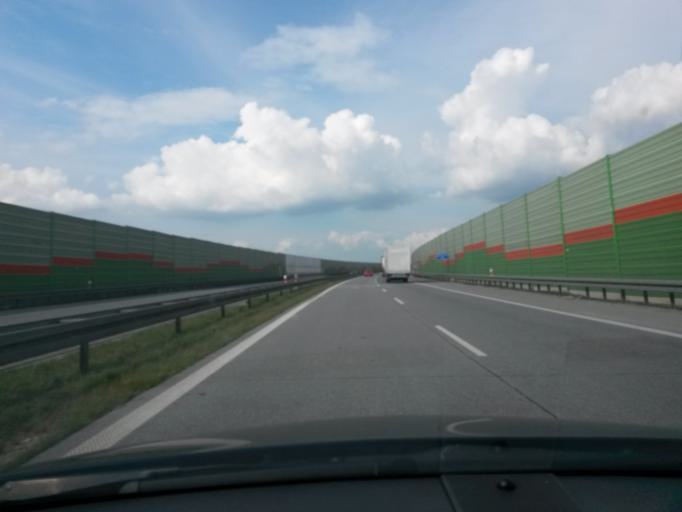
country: PL
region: Lodz Voivodeship
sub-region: Powiat tomaszowski
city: Lubochnia
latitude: 51.6051
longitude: 20.0608
